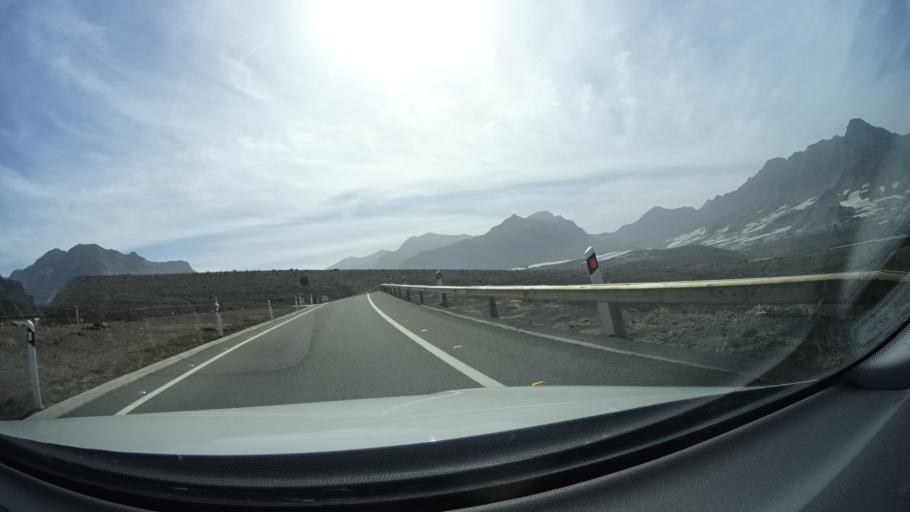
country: ES
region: Canary Islands
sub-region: Provincia de Las Palmas
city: San Nicolas
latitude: 28.0087
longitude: -15.7892
